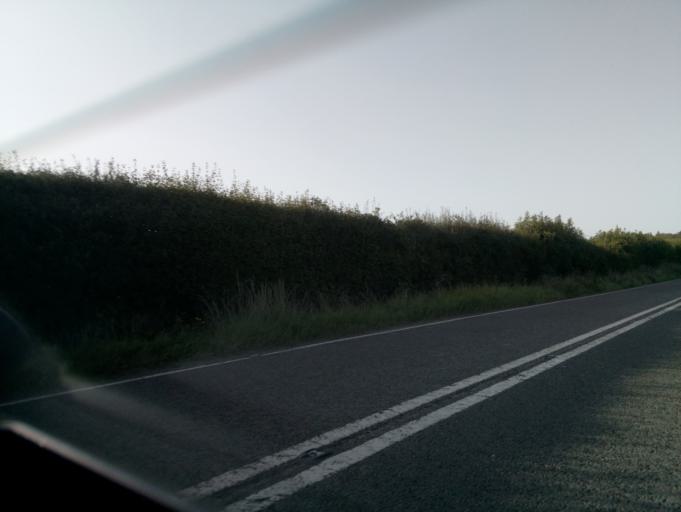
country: GB
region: England
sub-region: Gloucestershire
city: Gloucester
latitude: 51.9023
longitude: -2.2892
